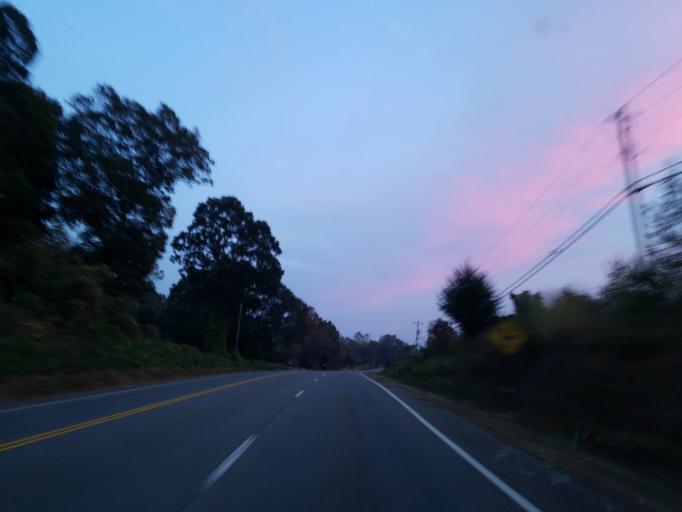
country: US
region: Georgia
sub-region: Pickens County
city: Jasper
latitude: 34.4905
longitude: -84.4614
